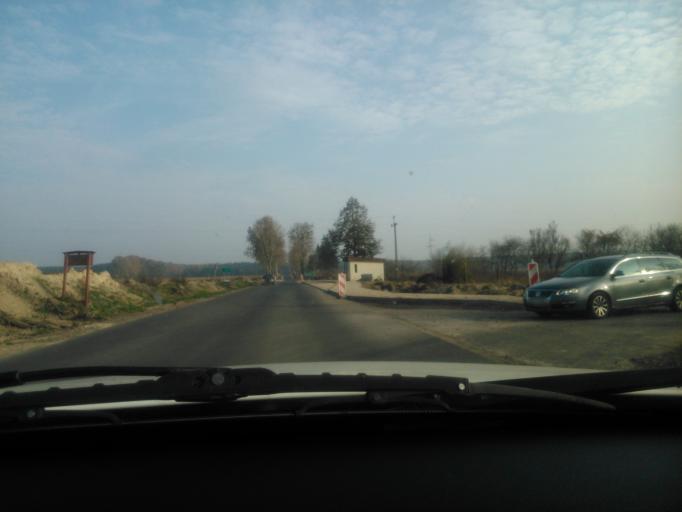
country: PL
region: Warmian-Masurian Voivodeship
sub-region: Powiat dzialdowski
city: Lidzbark
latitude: 53.2574
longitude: 19.8710
